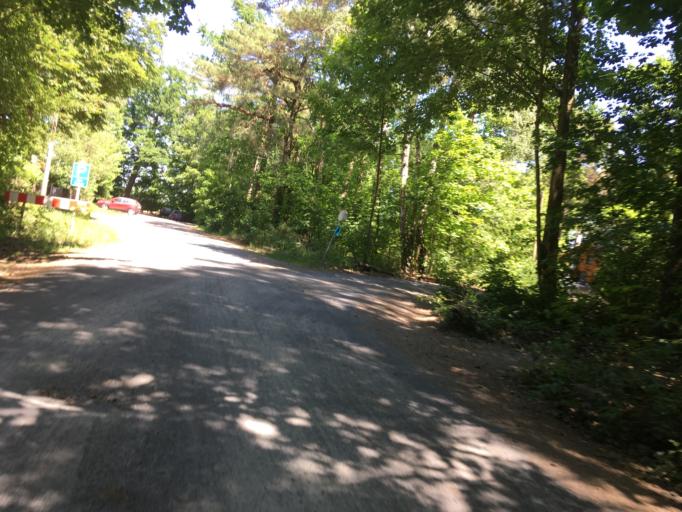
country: DE
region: Berlin
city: Schmockwitz
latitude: 52.3837
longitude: 13.6413
